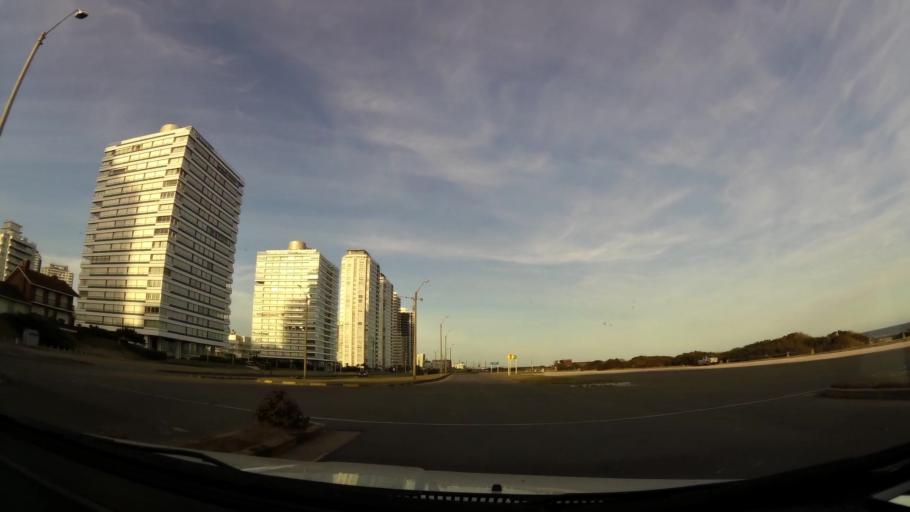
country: UY
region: Maldonado
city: Punta del Este
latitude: -34.9497
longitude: -54.9267
